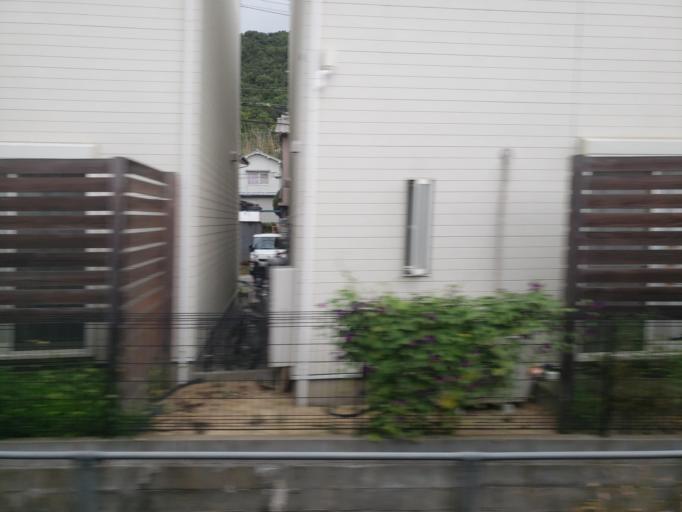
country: JP
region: Hyogo
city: Tatsunocho-tominaga
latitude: 34.8116
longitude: 134.6066
